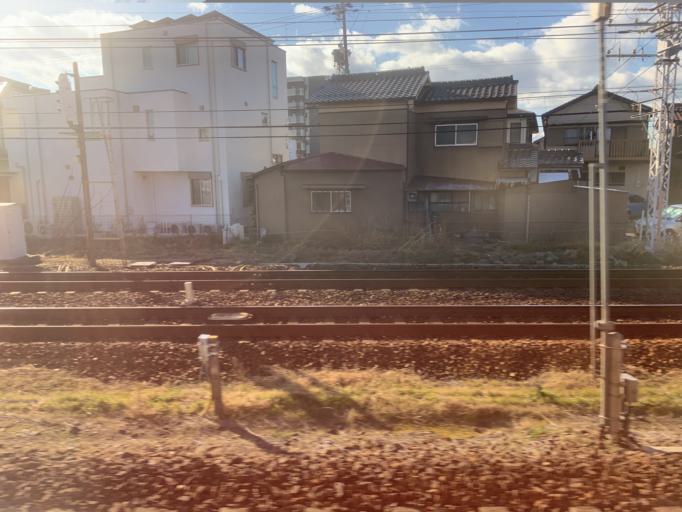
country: JP
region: Aichi
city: Ichinomiya
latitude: 35.3172
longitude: 136.7899
